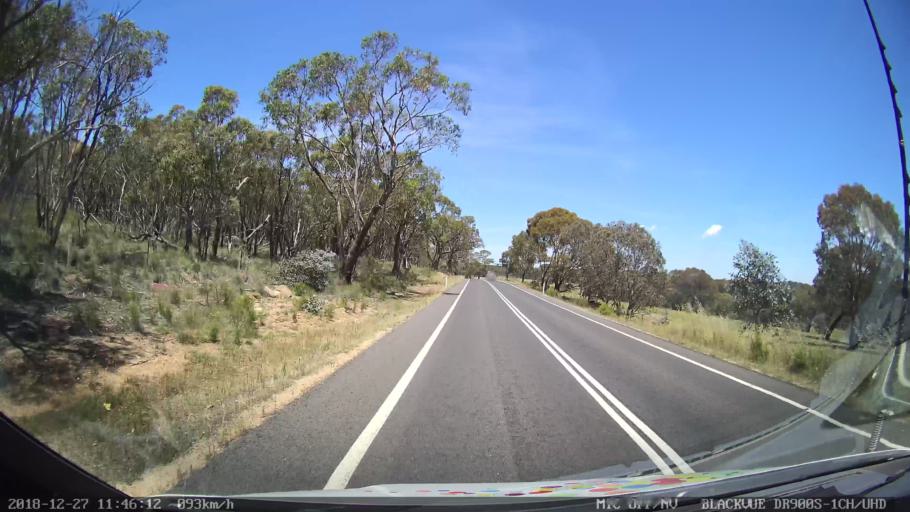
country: AU
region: New South Wales
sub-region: Bathurst Regional
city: Perthville
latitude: -33.5884
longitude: 149.4610
